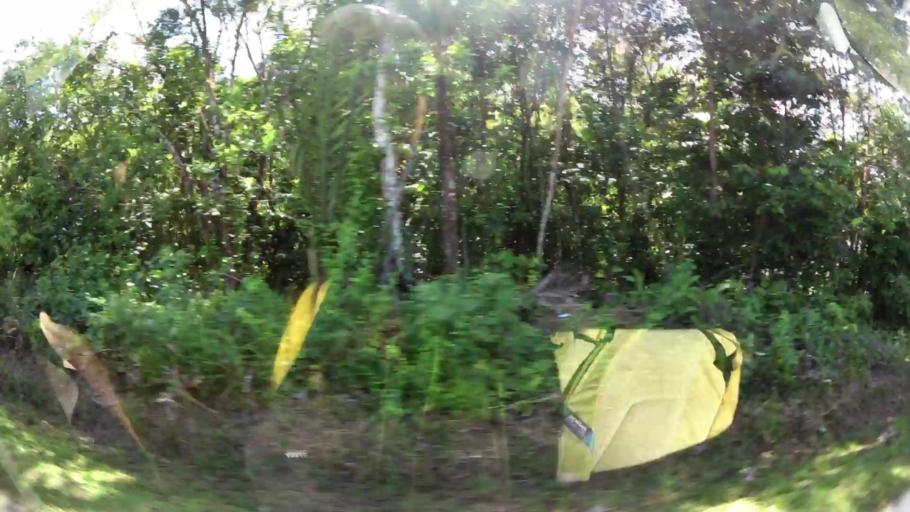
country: GF
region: Guyane
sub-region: Guyane
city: Matoury
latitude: 4.8438
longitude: -52.3292
